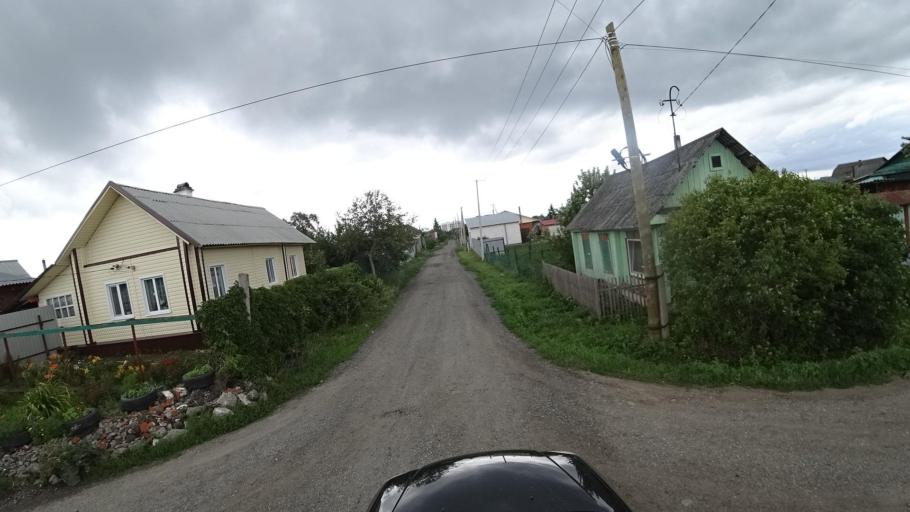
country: RU
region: Sverdlovsk
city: Kamyshlov
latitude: 56.8537
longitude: 62.6875
